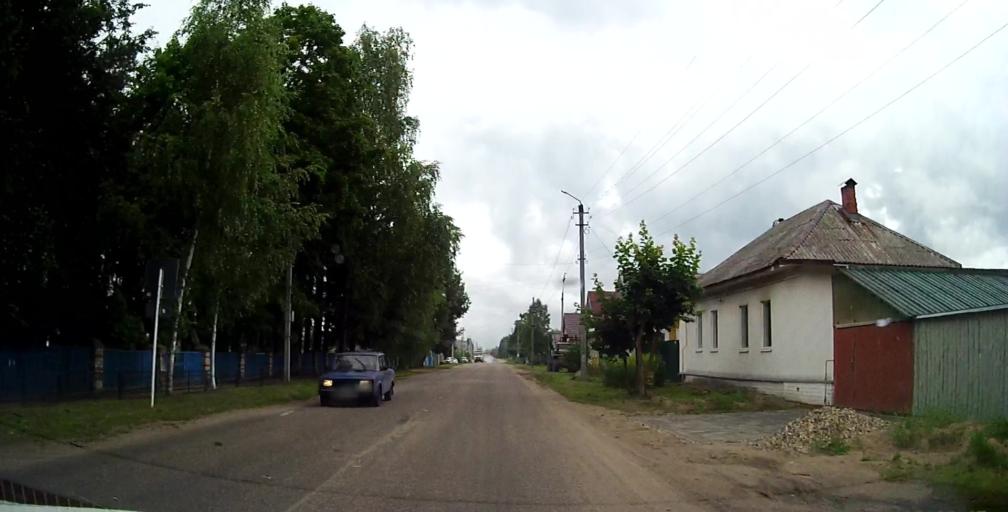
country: RU
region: Smolensk
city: Demidov
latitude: 55.2685
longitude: 31.5168
